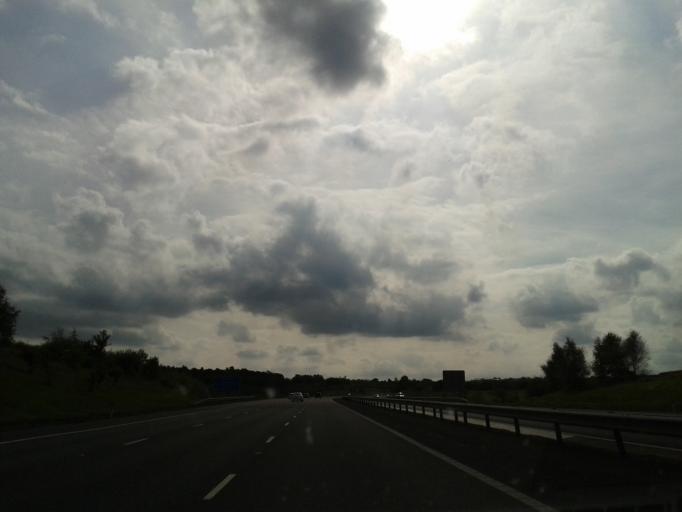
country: GB
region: England
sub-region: Staffordshire
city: Shenstone
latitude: 52.6125
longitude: -1.7982
